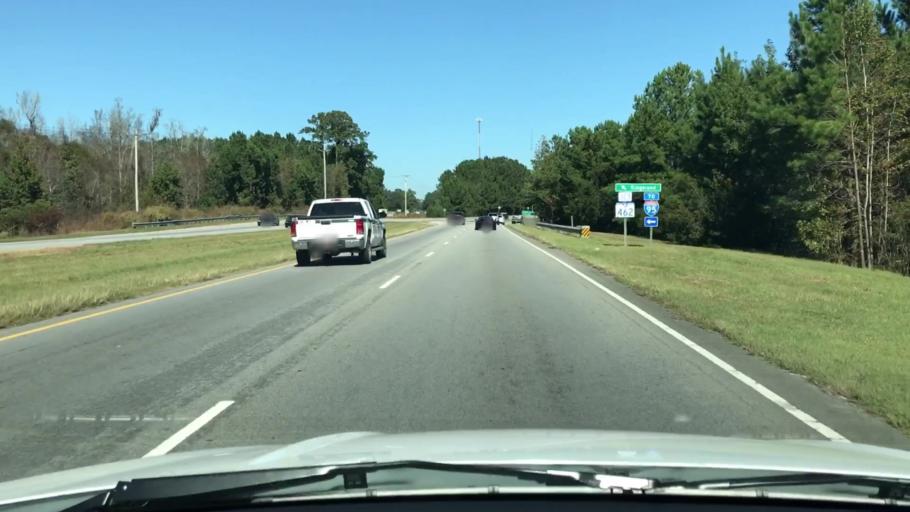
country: US
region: South Carolina
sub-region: Beaufort County
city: Bluffton
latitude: 32.3484
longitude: -80.9253
